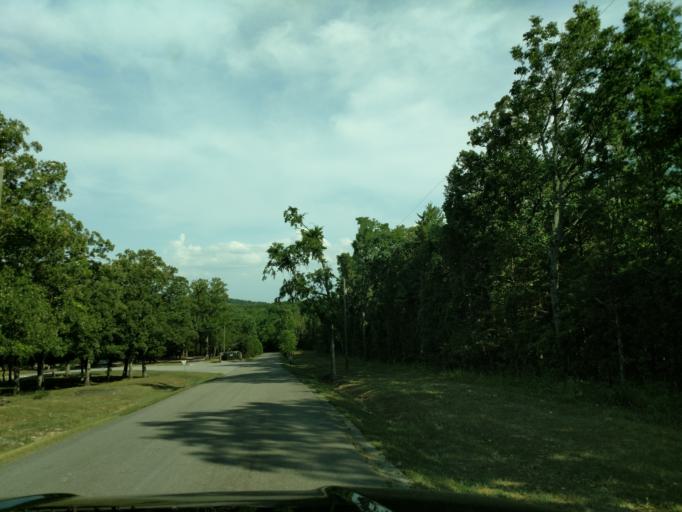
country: US
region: Missouri
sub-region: Barry County
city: Shell Knob
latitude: 36.5968
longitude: -93.5534
